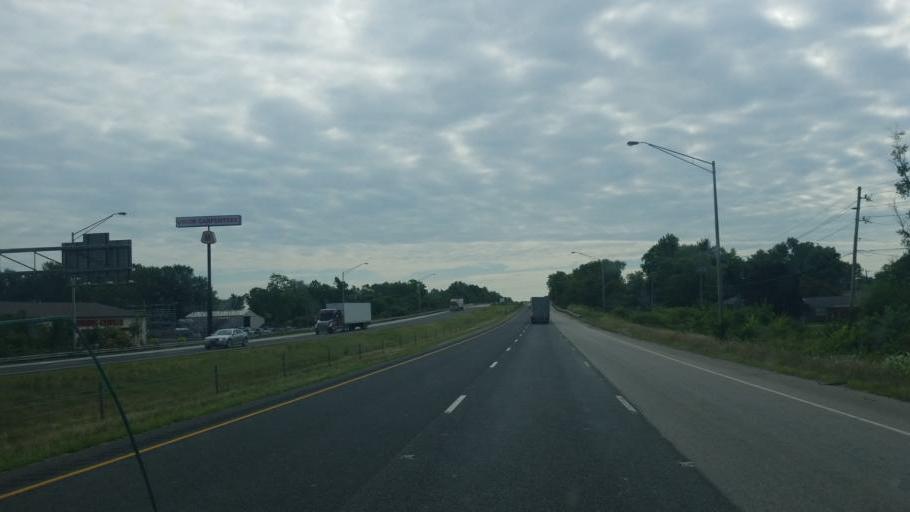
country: US
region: Indiana
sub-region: Vigo County
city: Terre Haute
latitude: 39.4307
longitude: -87.4107
